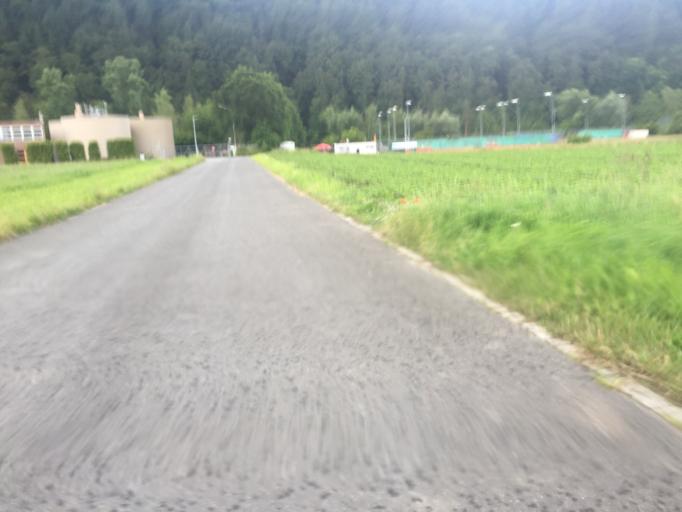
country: CH
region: Bern
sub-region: Bern-Mittelland District
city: Wohlen
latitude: 46.9624
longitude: 7.3753
